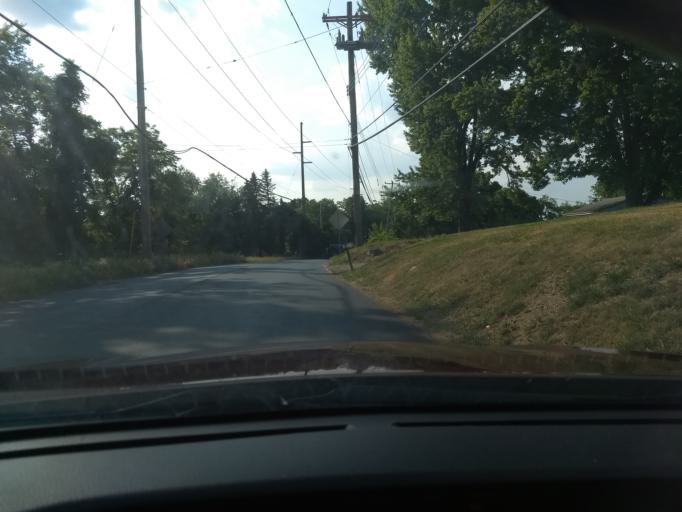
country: US
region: Pennsylvania
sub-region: Allegheny County
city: Plum
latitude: 40.4786
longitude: -79.7369
